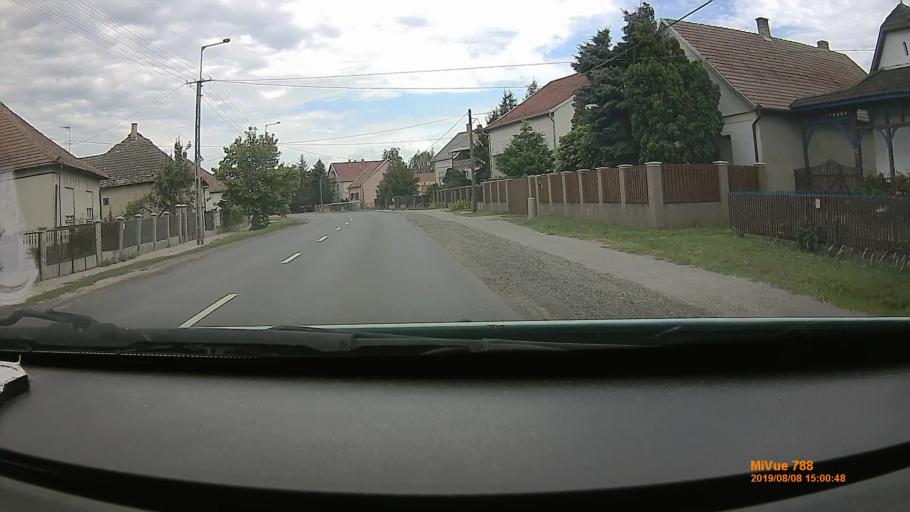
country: HU
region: Szabolcs-Szatmar-Bereg
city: Kocsord
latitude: 47.9389
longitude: 22.3815
